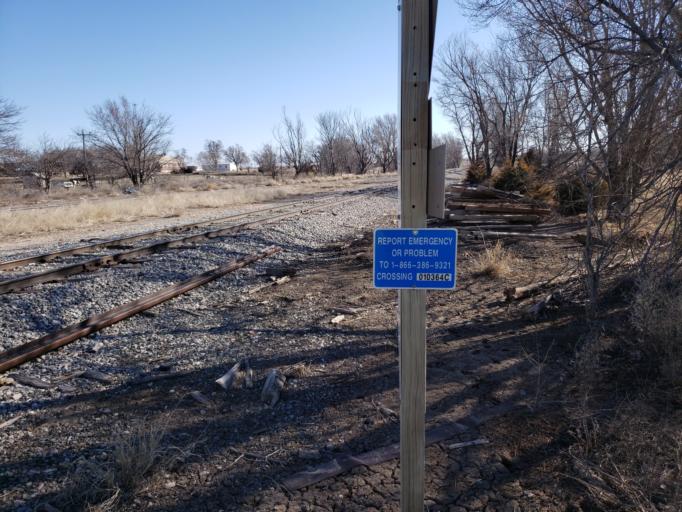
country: US
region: Kansas
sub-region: Lane County
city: Dighton
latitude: 38.4433
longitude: -100.1945
